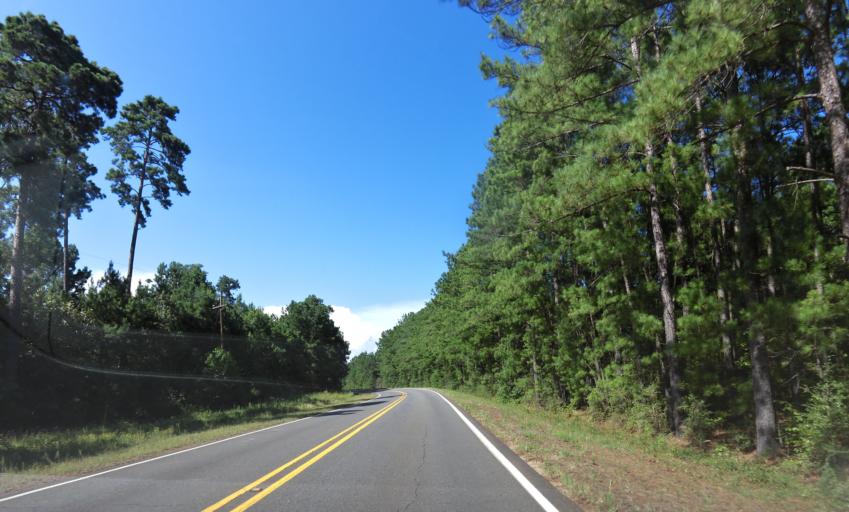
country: US
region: Louisiana
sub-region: Sabine Parish
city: Many
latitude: 31.3464
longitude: -93.5643
